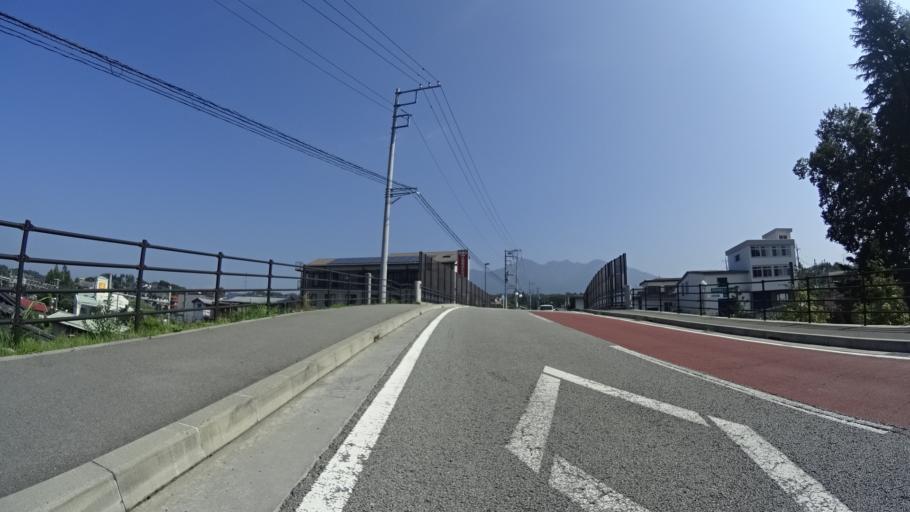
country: JP
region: Yamanashi
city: Nirasaki
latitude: 35.8628
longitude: 138.3193
